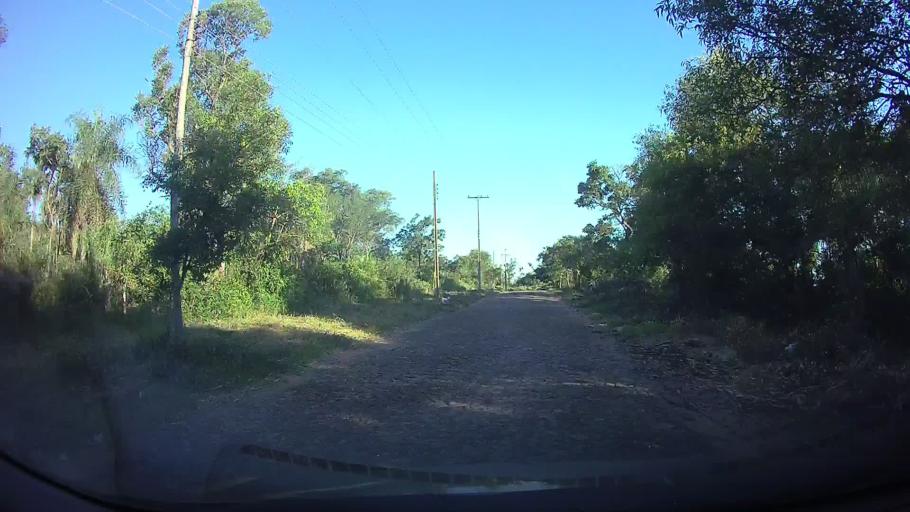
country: PY
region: Cordillera
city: San Bernardino
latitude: -25.3125
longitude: -57.2643
